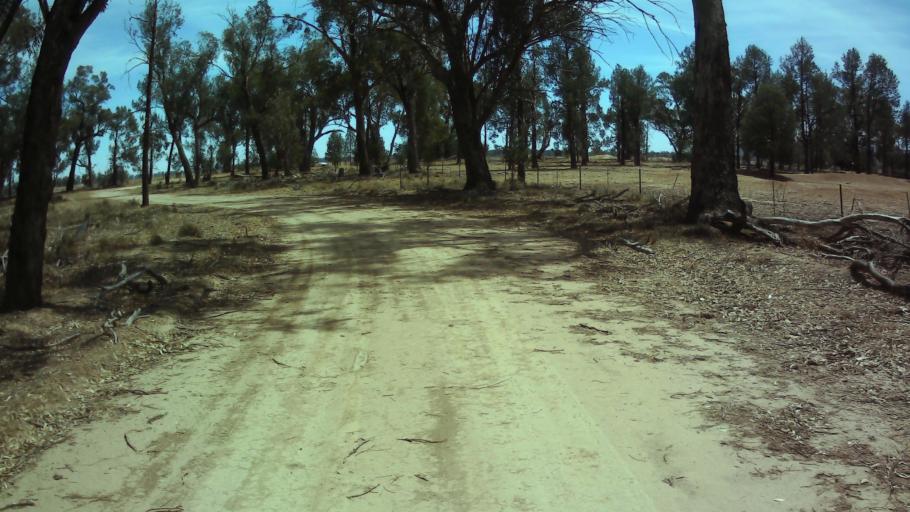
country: AU
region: New South Wales
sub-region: Weddin
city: Grenfell
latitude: -34.0329
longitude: 147.9333
